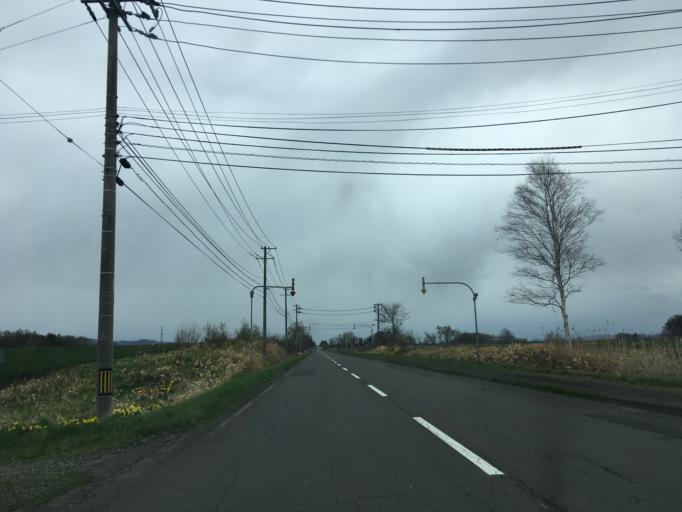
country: JP
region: Hokkaido
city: Chitose
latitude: 42.9065
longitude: 141.8122
